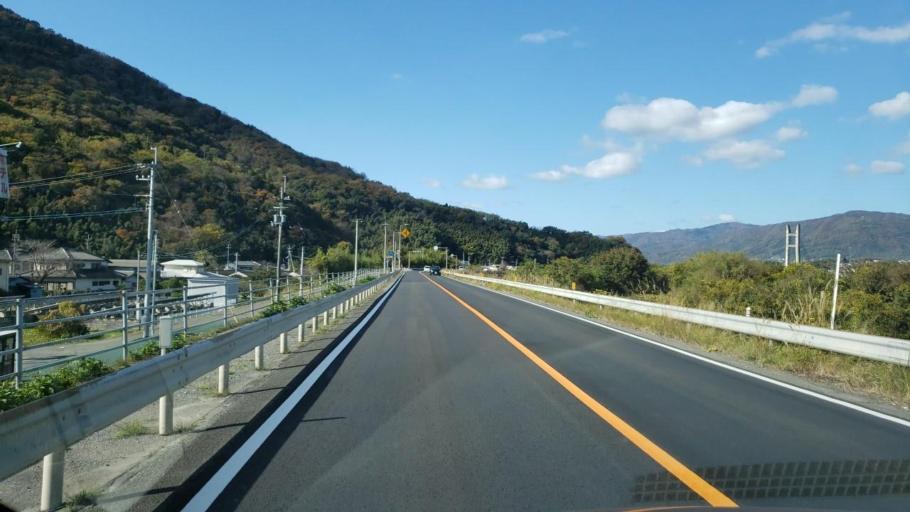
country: JP
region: Tokushima
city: Wakimachi
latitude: 34.0624
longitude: 134.2025
